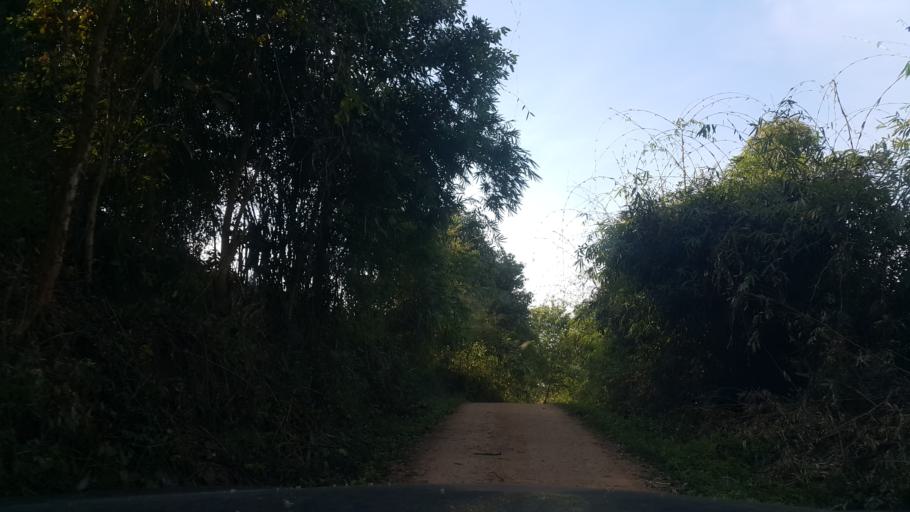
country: TH
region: Chiang Mai
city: Samoeng
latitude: 18.9584
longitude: 98.6735
